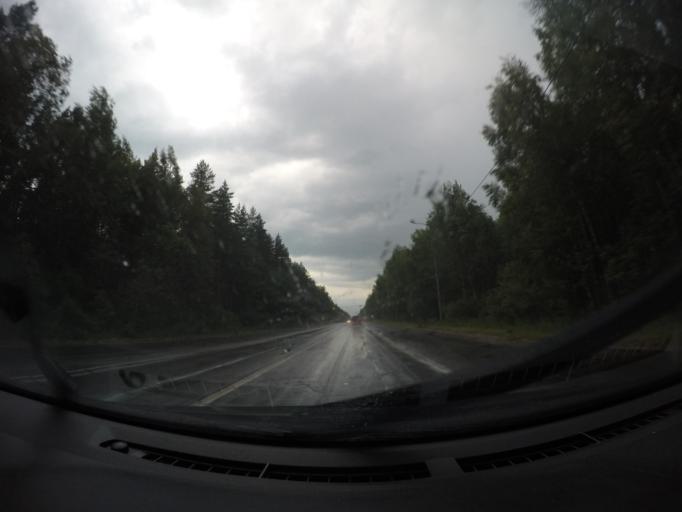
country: RU
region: Moskovskaya
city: Il'inskiy Pogost
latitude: 55.4579
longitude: 38.9889
